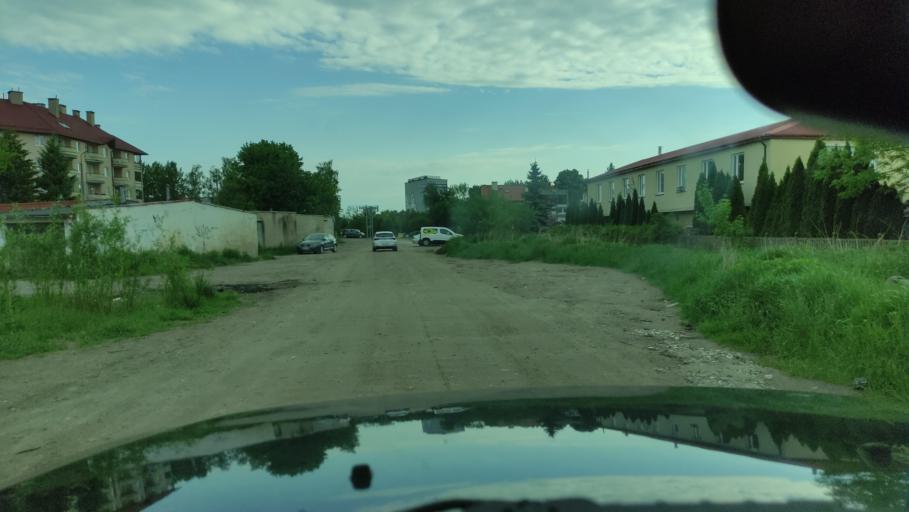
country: PL
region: Warmian-Masurian Voivodeship
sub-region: Powiat olsztynski
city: Olsztyn
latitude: 53.7679
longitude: 20.5104
